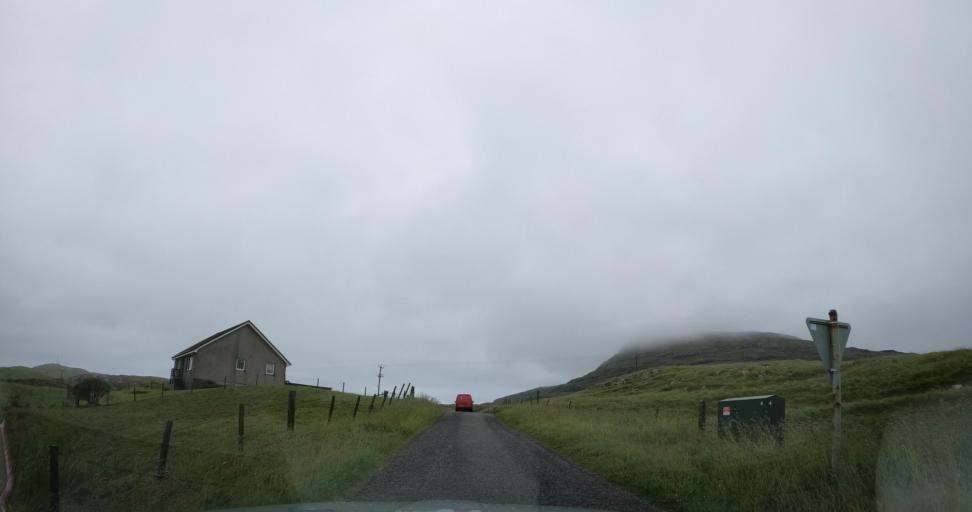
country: GB
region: Scotland
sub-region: Eilean Siar
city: Barra
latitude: 57.0020
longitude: -7.4800
